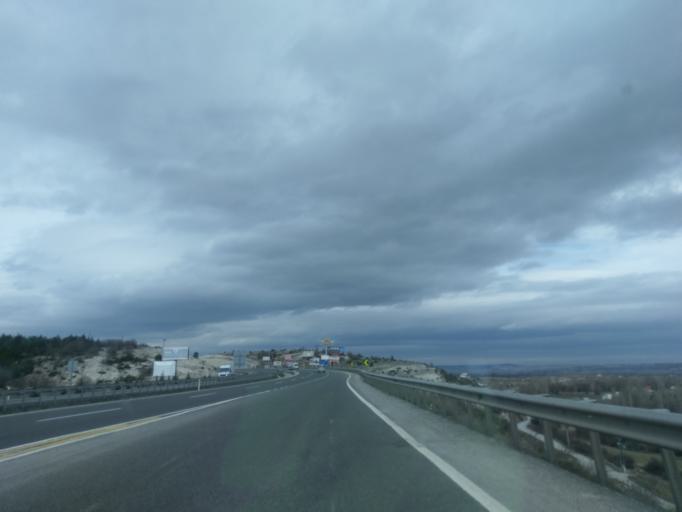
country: TR
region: Kuetahya
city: Kutahya
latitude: 39.3716
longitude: 30.0667
